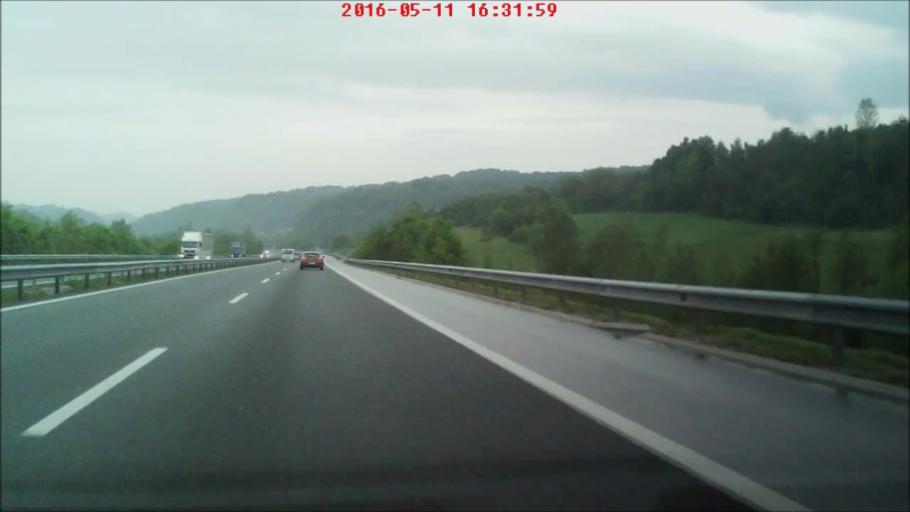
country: SI
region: Sentilj
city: Sentilj v Slov. Goricah
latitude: 46.6550
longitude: 15.6479
